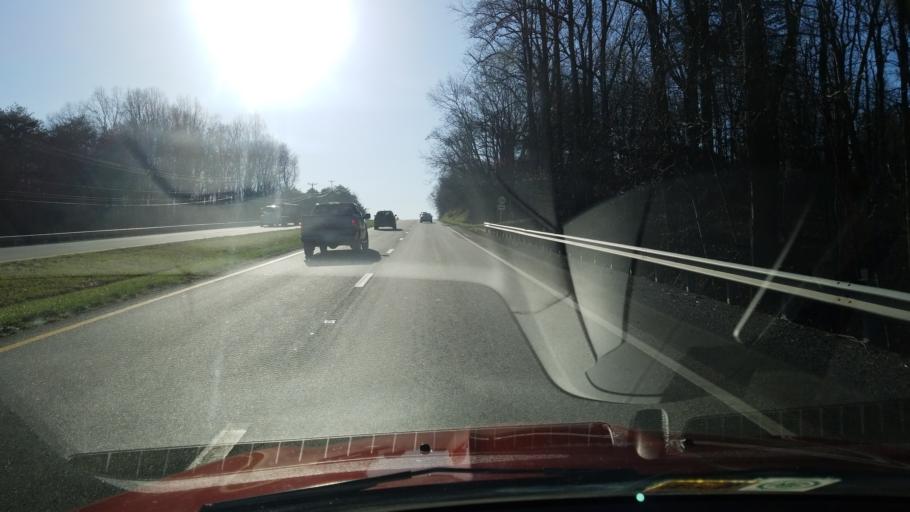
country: US
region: Virginia
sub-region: Franklin County
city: Rocky Mount
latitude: 37.0868
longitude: -79.9311
